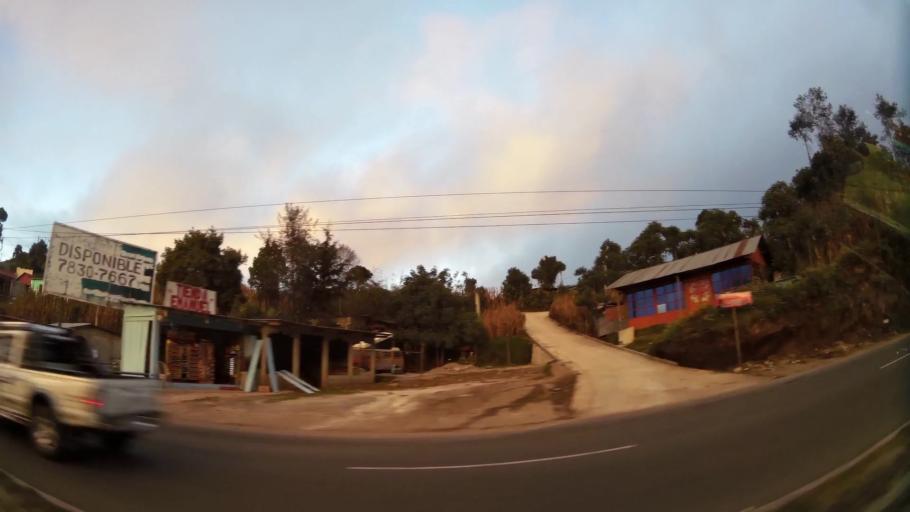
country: GT
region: Solola
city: Concepcion
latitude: 14.8502
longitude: -91.1460
